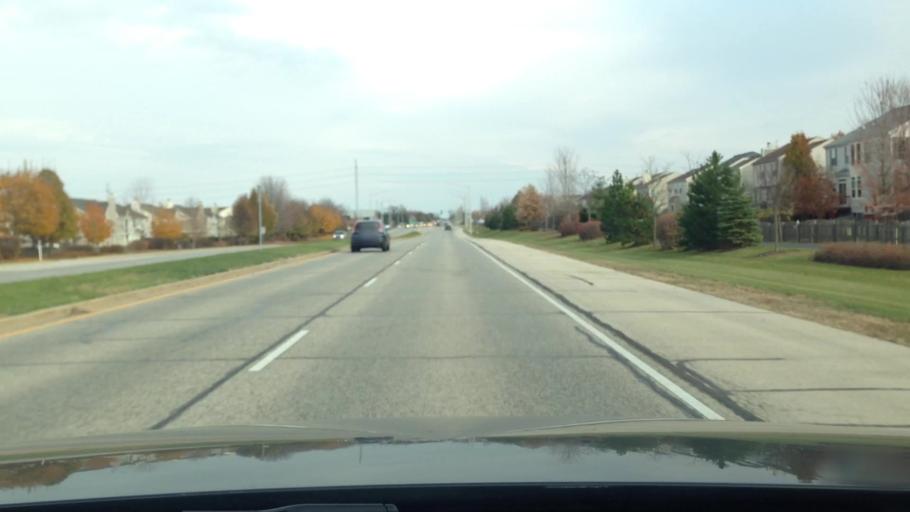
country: US
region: Illinois
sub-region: McHenry County
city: Huntley
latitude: 42.1755
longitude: -88.4084
